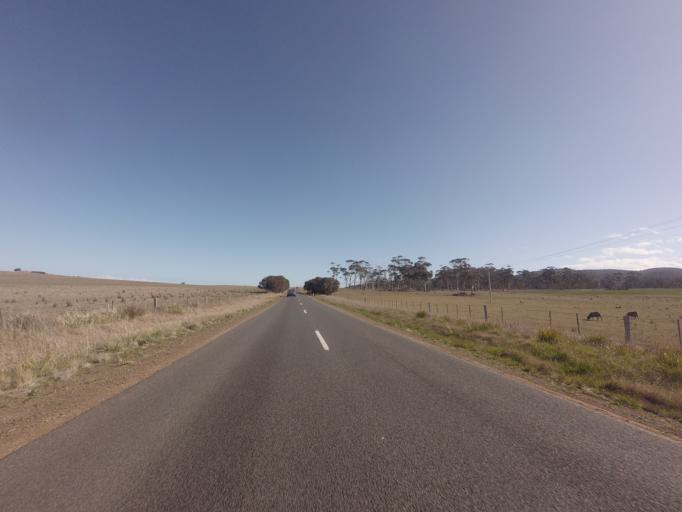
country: AU
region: Tasmania
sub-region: Sorell
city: Sorell
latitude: -42.2081
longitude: 148.0408
